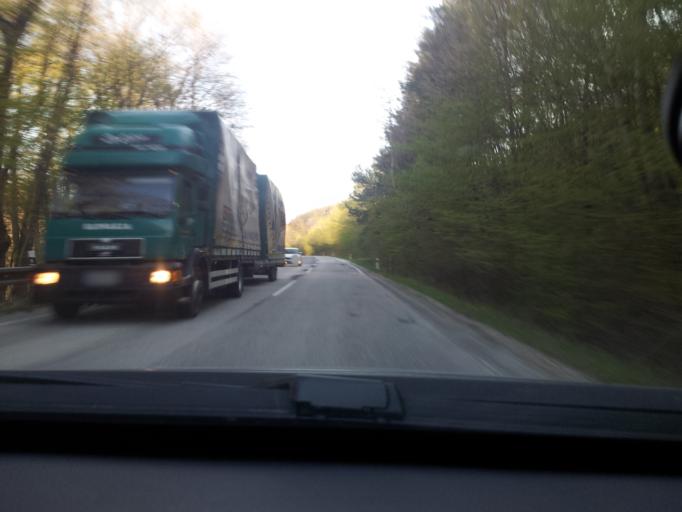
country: SK
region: Nitriansky
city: Zlate Moravce
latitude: 48.4837
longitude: 18.4185
